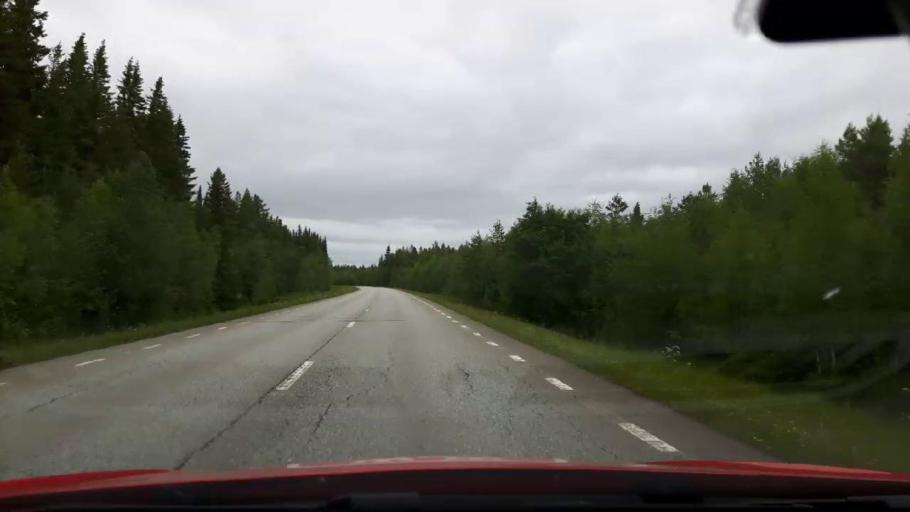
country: SE
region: Jaemtland
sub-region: OEstersunds Kommun
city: Lit
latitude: 63.6028
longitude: 14.6656
